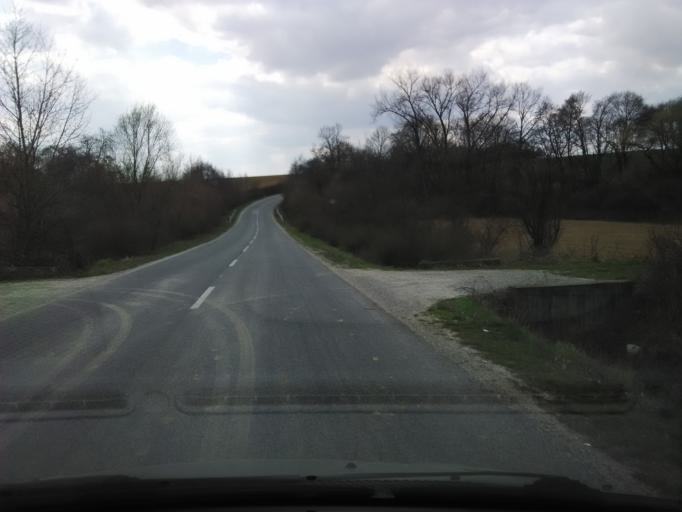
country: SK
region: Nitriansky
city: Zlate Moravce
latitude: 48.4205
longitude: 18.3180
